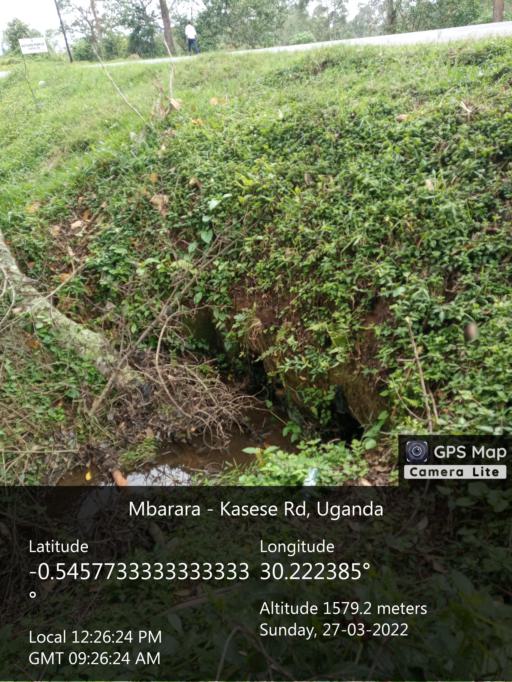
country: UG
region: Western Region
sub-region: Bushenyi District
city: Bushenyi
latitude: -0.5458
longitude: 30.2224
